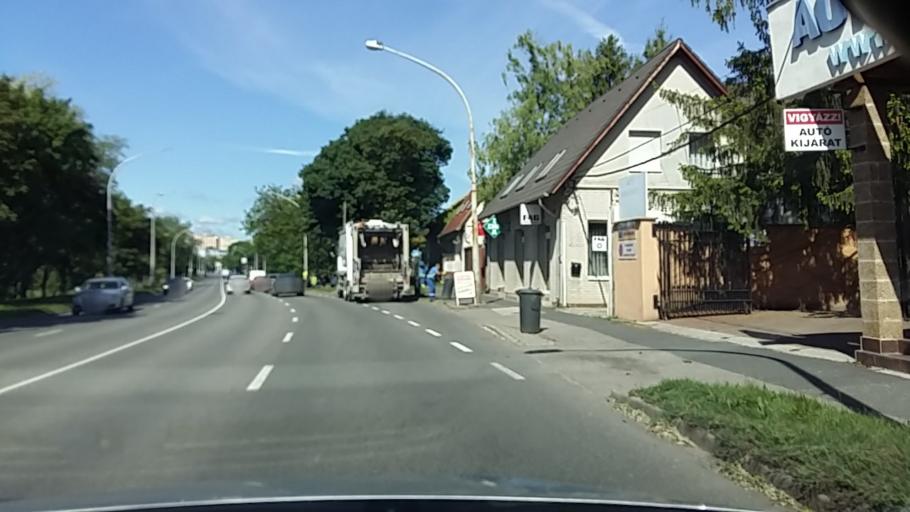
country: HU
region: Fejer
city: Szekesfehervar
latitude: 47.1951
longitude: 18.4381
